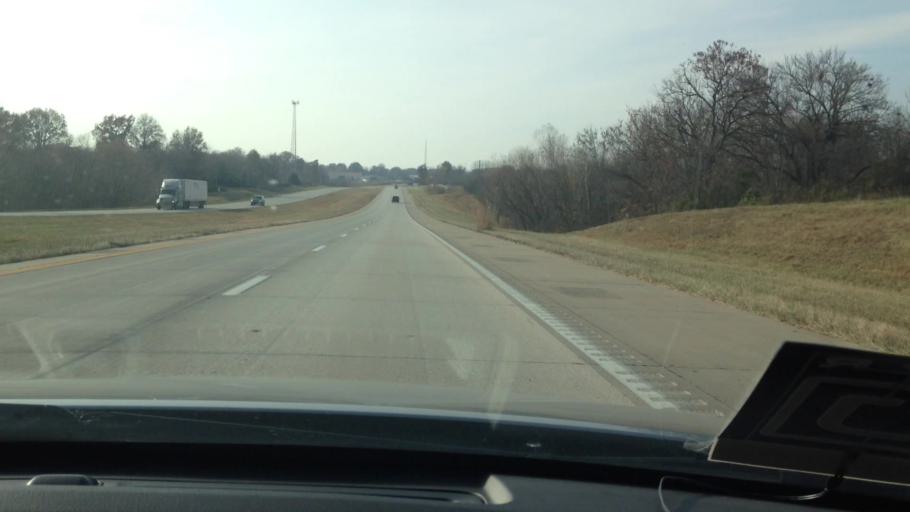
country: US
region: Missouri
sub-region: Henry County
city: Clinton
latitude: 38.4641
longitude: -93.9841
